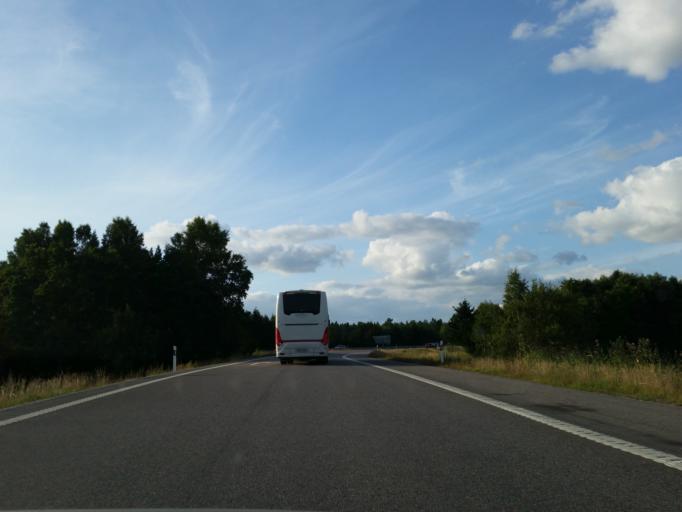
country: SE
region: Stockholm
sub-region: Sodertalje Kommun
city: Pershagen
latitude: 59.0890
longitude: 17.6012
